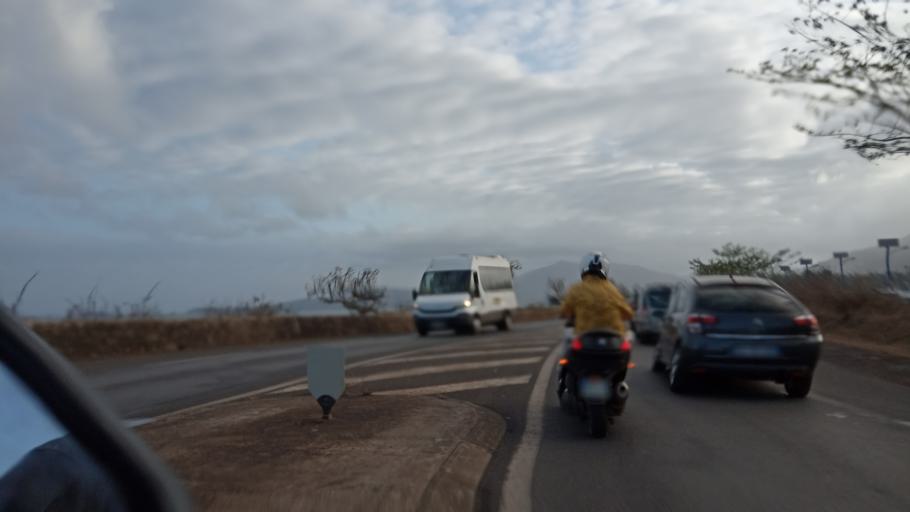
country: YT
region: Mamoudzou
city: Mamoudzou
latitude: -12.7880
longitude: 45.2252
